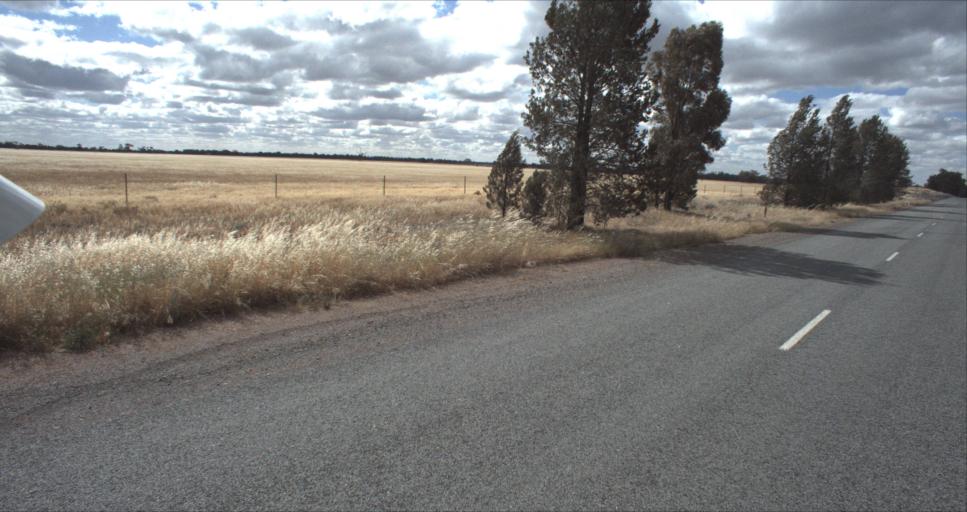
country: AU
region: New South Wales
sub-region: Leeton
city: Leeton
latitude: -34.6761
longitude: 146.3465
